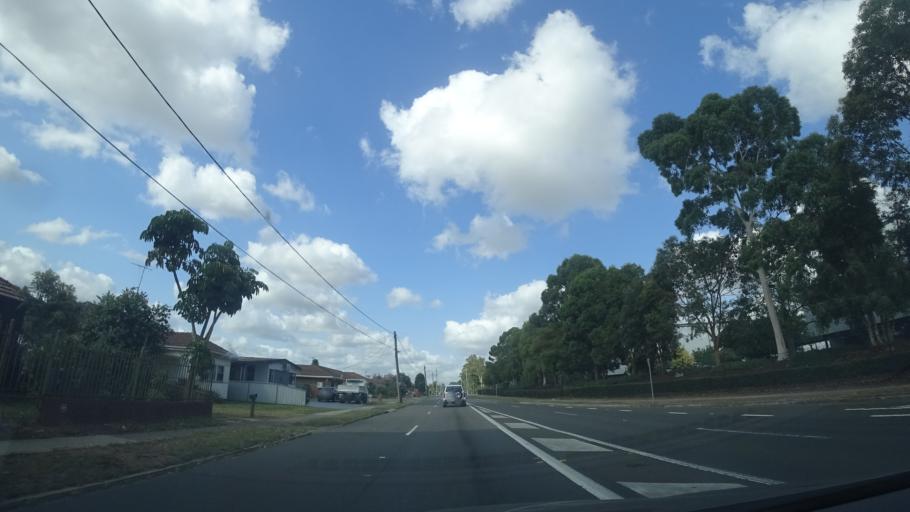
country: AU
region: New South Wales
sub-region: Fairfield
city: Liverpool
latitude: -33.9311
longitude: 150.9301
